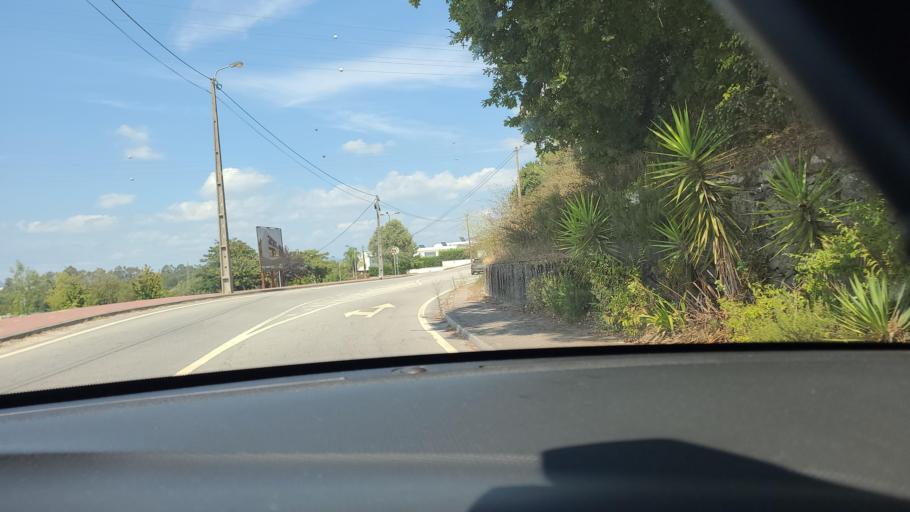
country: PT
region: Braga
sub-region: Braga
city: Adaufe
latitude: 41.5749
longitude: -8.4184
